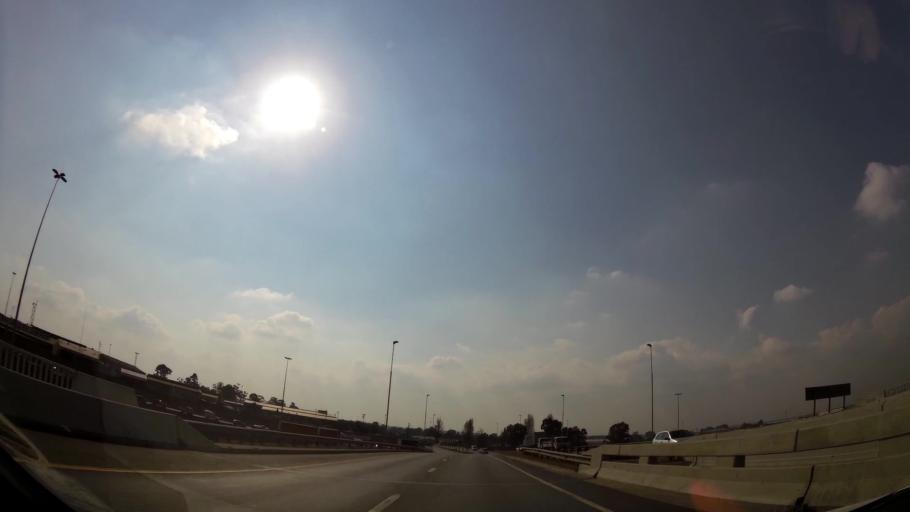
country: ZA
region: Gauteng
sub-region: Ekurhuleni Metropolitan Municipality
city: Germiston
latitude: -26.1754
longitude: 28.1987
